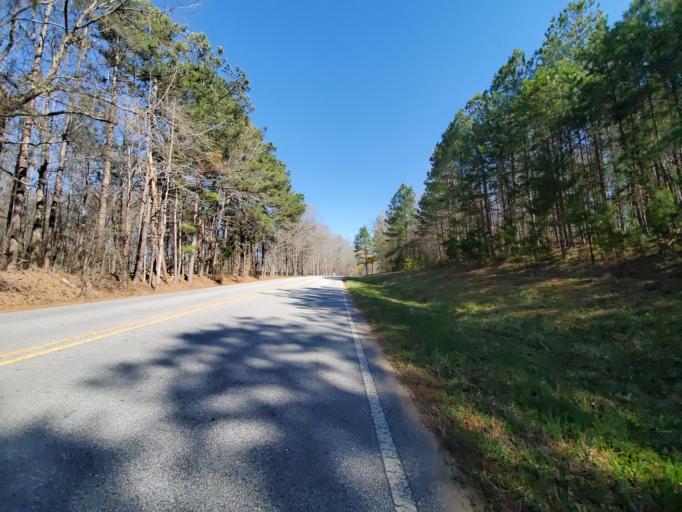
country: US
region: Georgia
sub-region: Oconee County
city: Bogart
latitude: 34.0017
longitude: -83.4953
